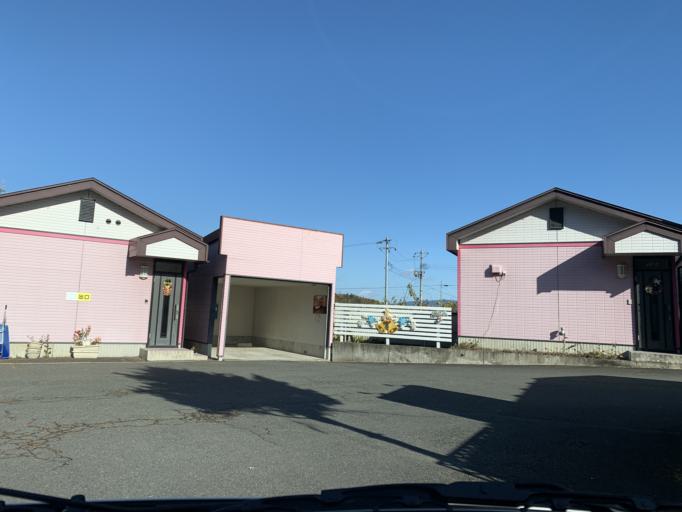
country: JP
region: Iwate
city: Mizusawa
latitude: 39.0905
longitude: 141.1198
